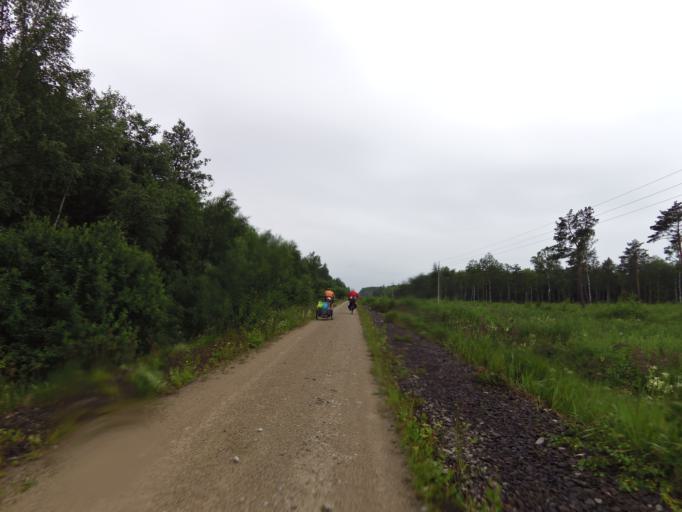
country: EE
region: Harju
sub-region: Nissi vald
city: Turba
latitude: 58.9864
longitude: 23.9325
